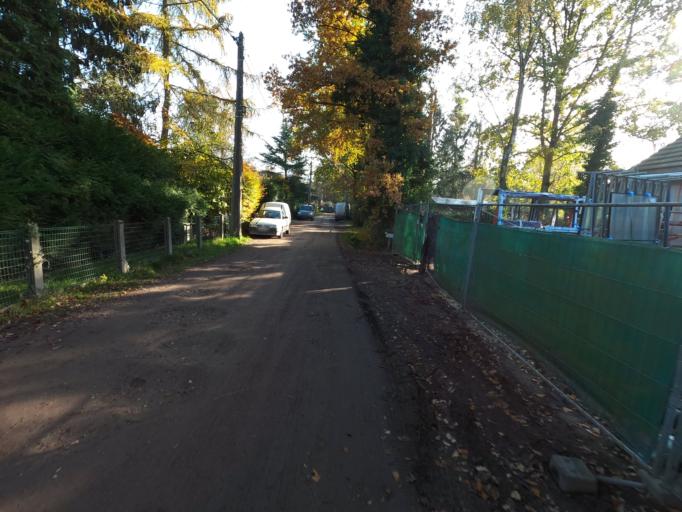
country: BE
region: Flanders
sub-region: Provincie Antwerpen
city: Wuustwezel
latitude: 51.3435
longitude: 4.5452
